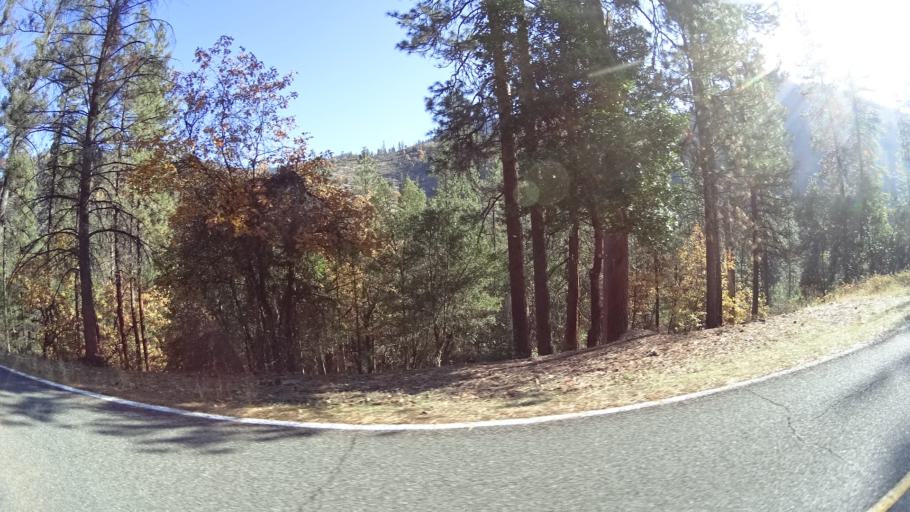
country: US
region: California
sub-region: Siskiyou County
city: Yreka
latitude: 41.8921
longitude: -122.8232
